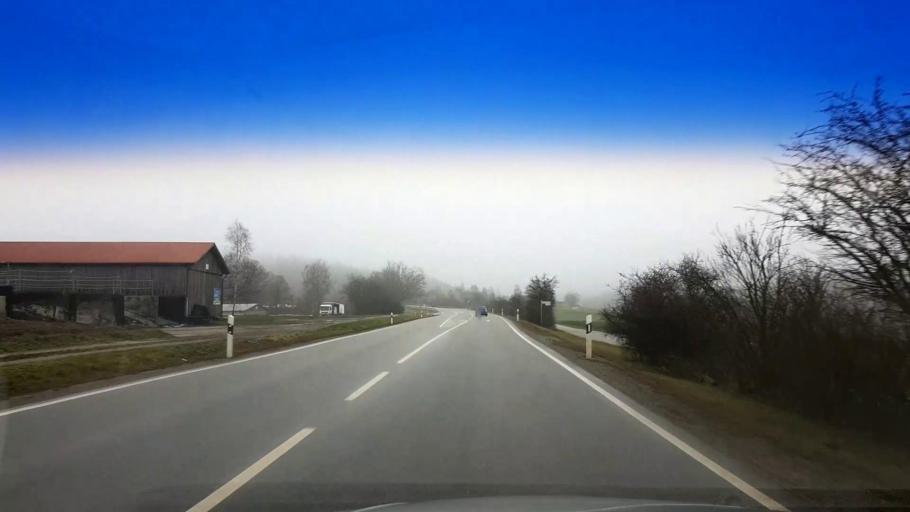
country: DE
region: Bavaria
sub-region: Upper Palatinate
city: Wiesau
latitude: 49.8645
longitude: 12.2507
